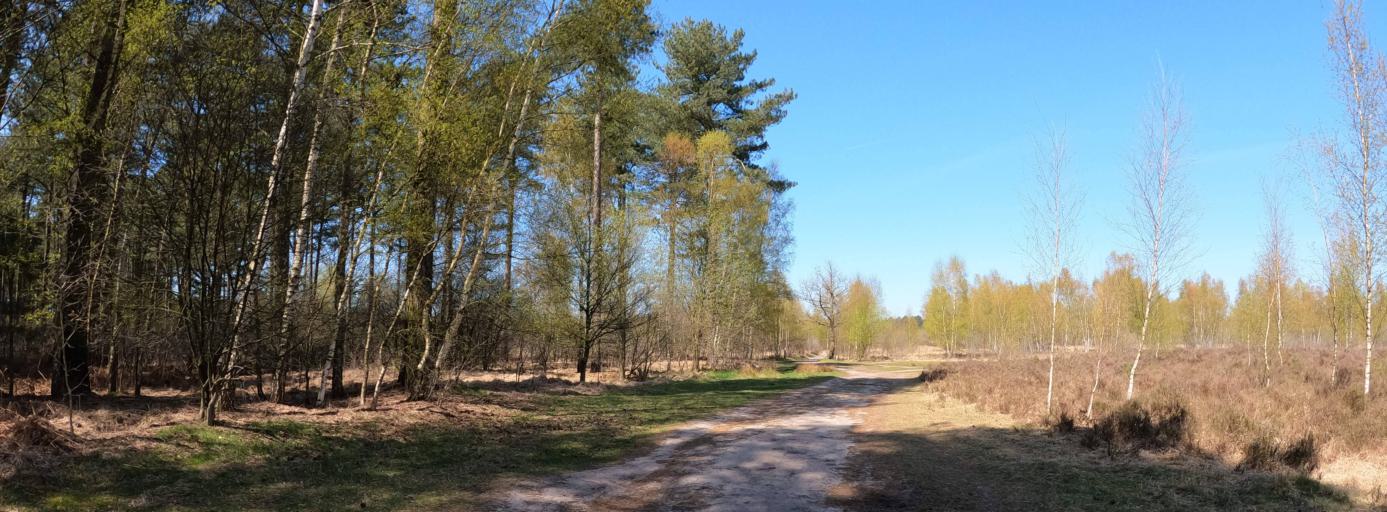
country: BE
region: Flanders
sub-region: Provincie Antwerpen
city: Kalmthout
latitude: 51.3445
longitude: 4.4875
